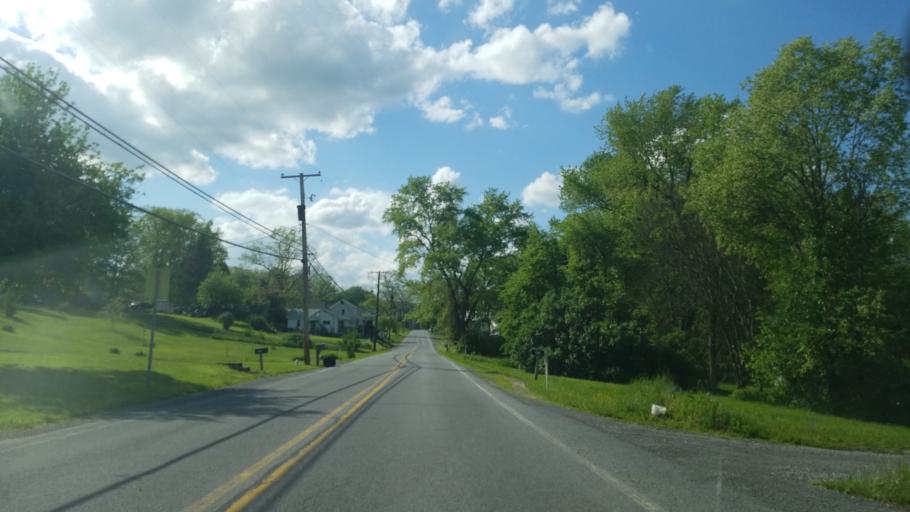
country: US
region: Pennsylvania
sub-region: Clearfield County
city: Troy
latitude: 40.9218
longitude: -78.2727
